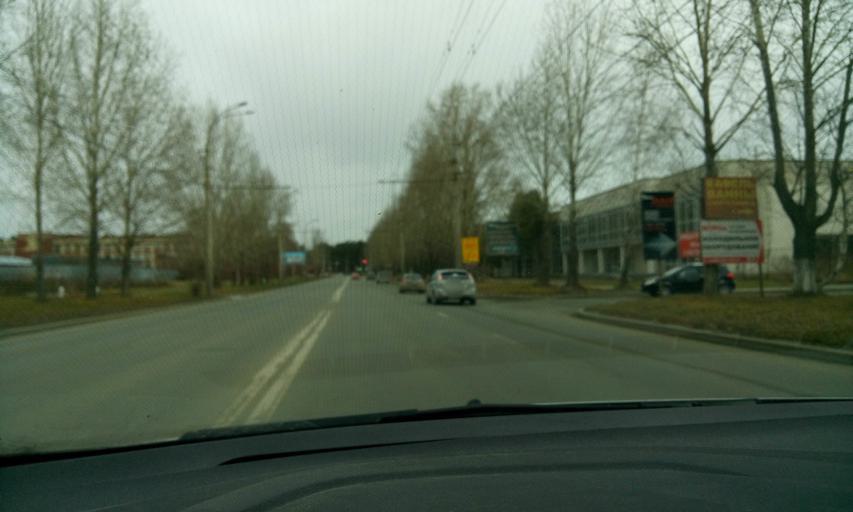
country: RU
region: Sverdlovsk
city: Sovkhoznyy
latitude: 56.7778
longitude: 60.5550
